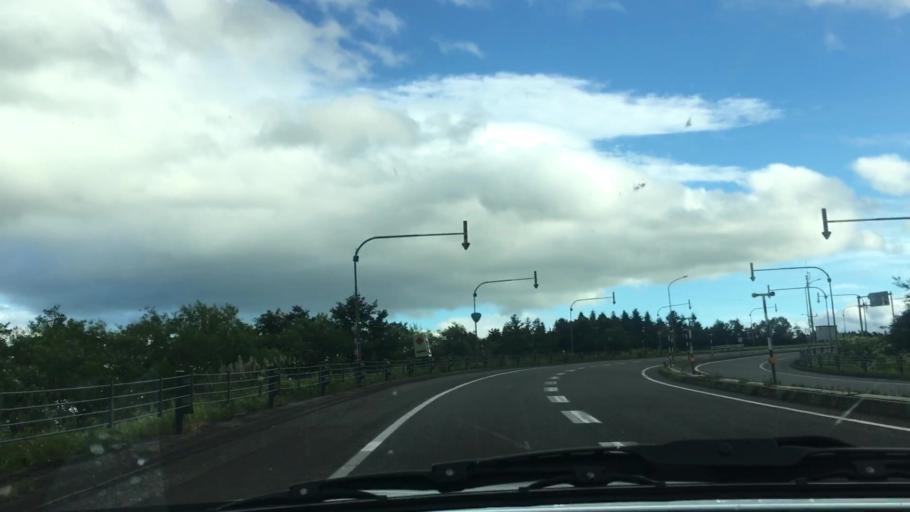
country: JP
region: Hokkaido
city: Otofuke
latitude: 43.1625
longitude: 142.8039
